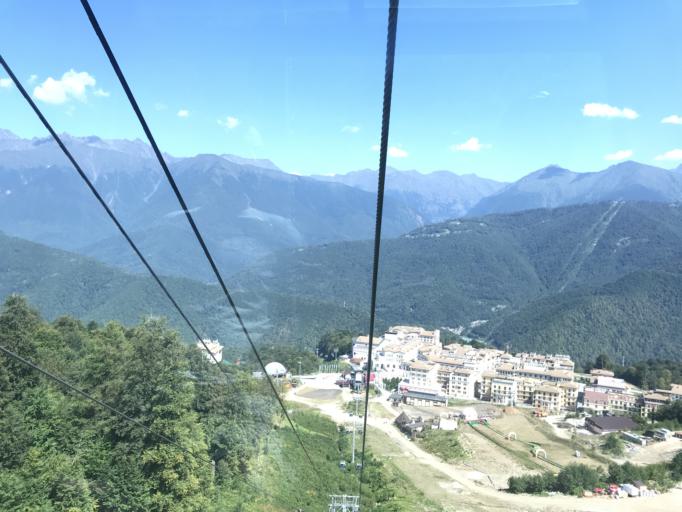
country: RU
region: Krasnodarskiy
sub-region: Sochi City
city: Krasnaya Polyana
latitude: 43.6651
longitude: 40.2559
